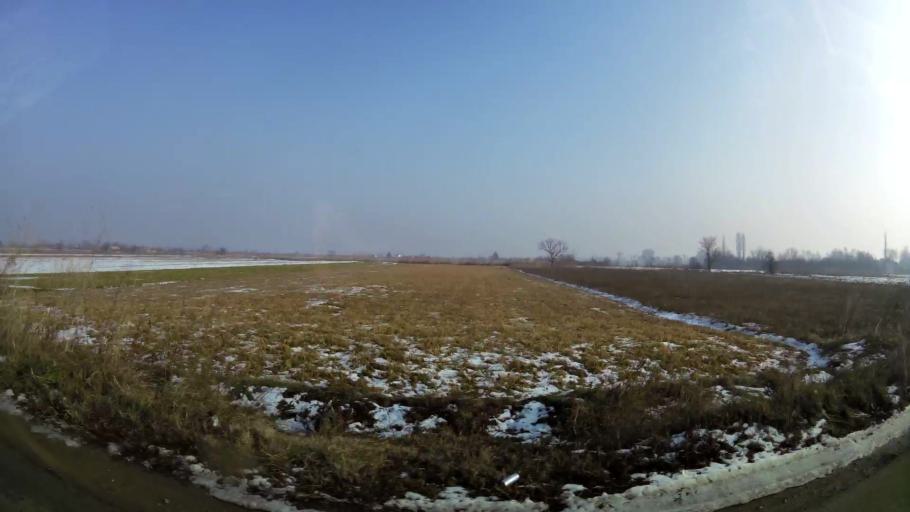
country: MK
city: Kadino
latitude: 41.9492
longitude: 21.5974
